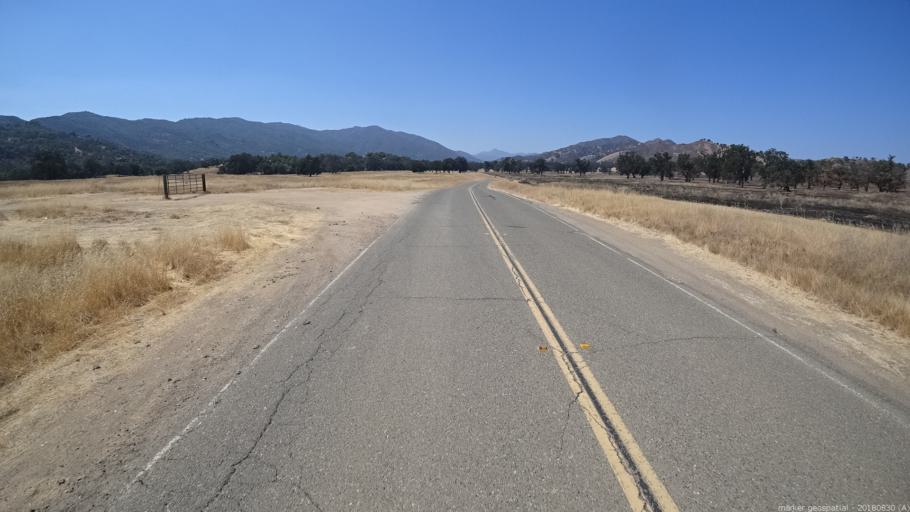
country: US
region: California
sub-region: Monterey County
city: King City
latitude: 35.9698
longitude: -121.3154
